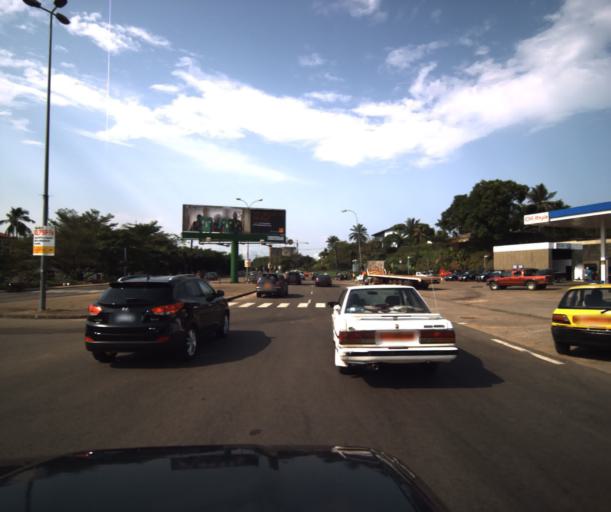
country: CM
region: Littoral
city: Douala
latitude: 4.0366
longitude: 9.6903
